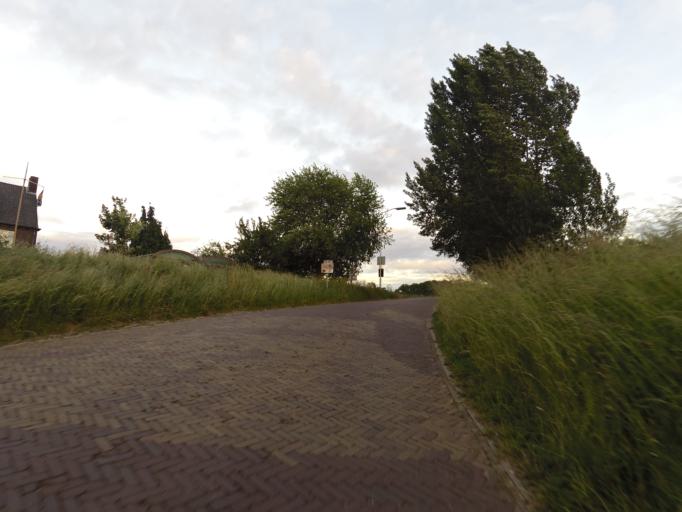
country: NL
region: Gelderland
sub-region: Gemeente Duiven
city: Duiven
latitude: 51.8931
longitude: 6.0259
